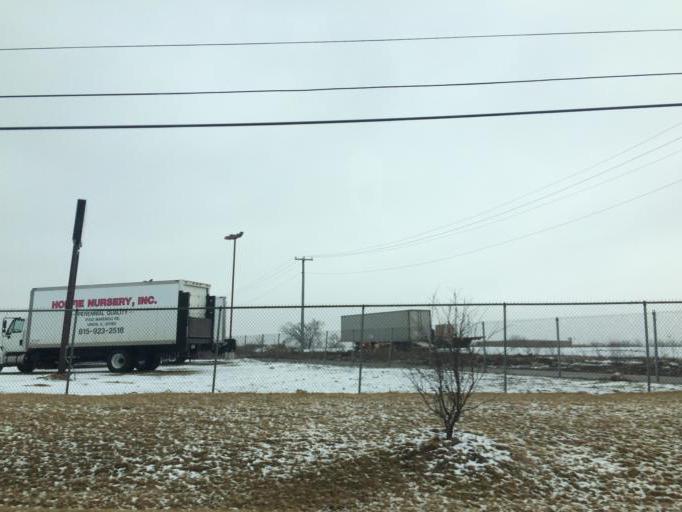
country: US
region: Illinois
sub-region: McHenry County
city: Huntley
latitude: 42.1562
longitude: -88.4312
